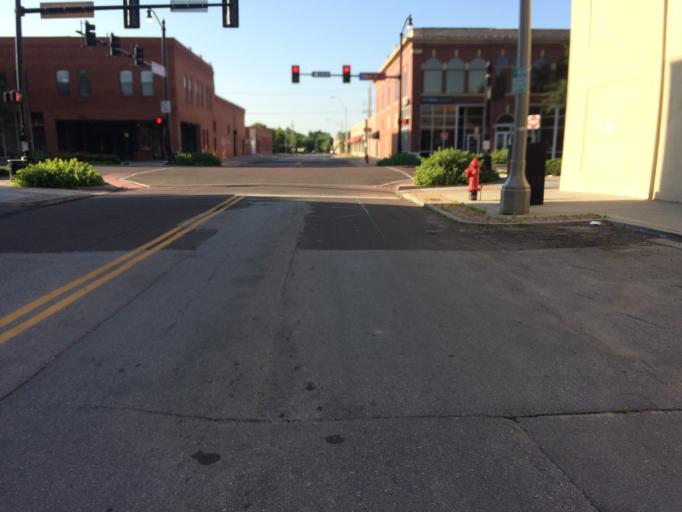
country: US
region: Oklahoma
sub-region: Cleveland County
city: Norman
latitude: 35.2224
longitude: -97.4407
